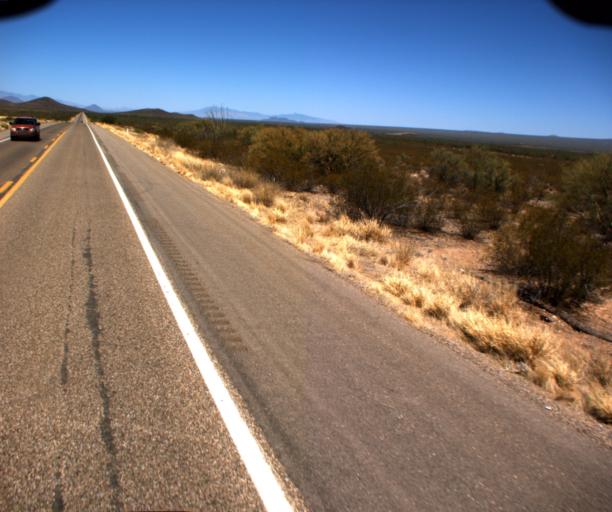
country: US
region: Arizona
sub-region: Pima County
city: Three Points
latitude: 32.0453
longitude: -111.4336
